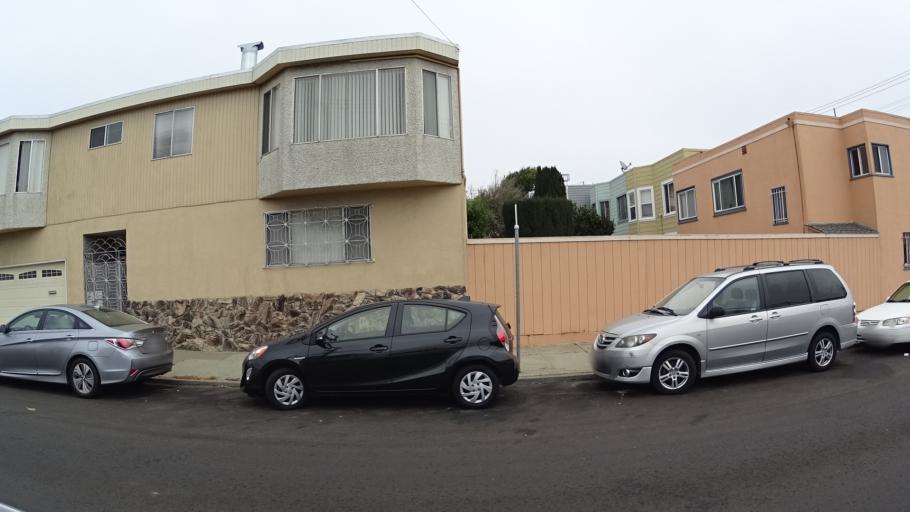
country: US
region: California
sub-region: San Mateo County
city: Brisbane
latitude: 37.7123
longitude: -122.4109
